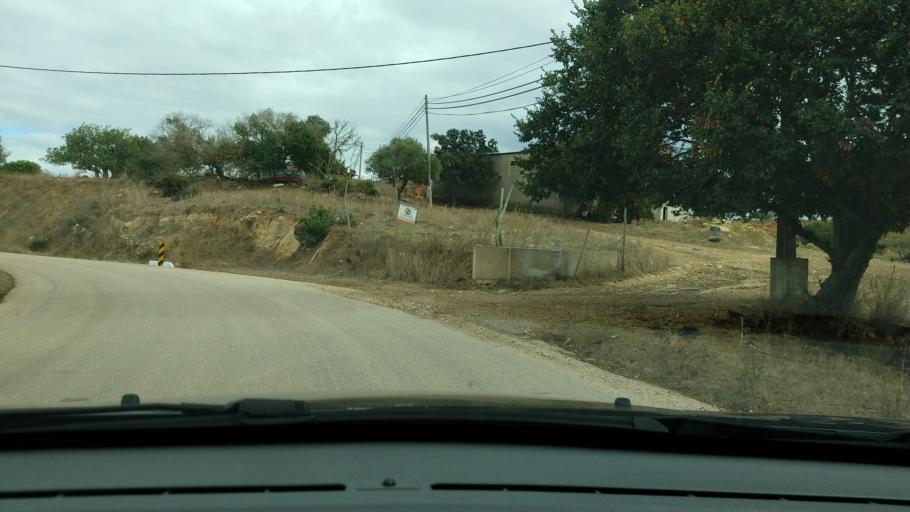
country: PT
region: Faro
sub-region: Lagos
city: Lagos
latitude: 37.0855
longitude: -8.7801
